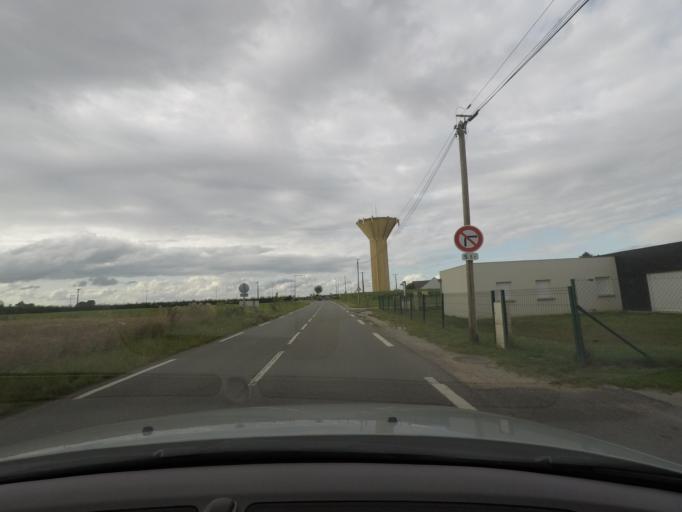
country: FR
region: Haute-Normandie
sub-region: Departement de la Seine-Maritime
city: Ymare
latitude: 49.3545
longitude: 1.1830
